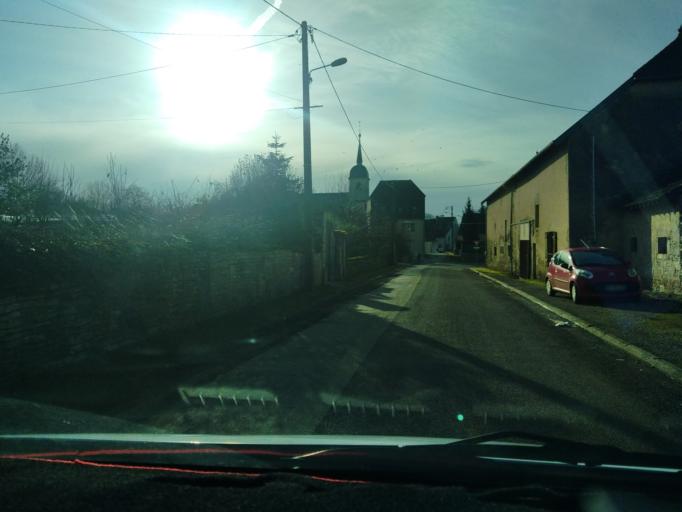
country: FR
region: Franche-Comte
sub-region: Departement de la Haute-Saone
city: Marnay
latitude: 47.3216
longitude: 5.6843
